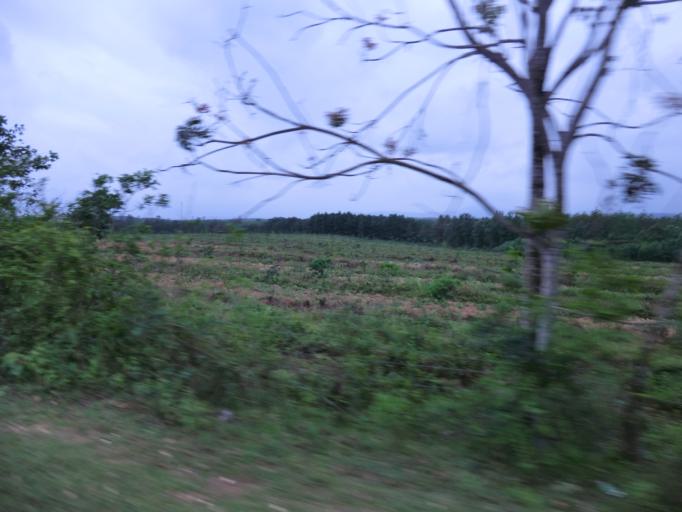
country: VN
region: Quang Tri
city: Cam Lo
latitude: 16.8893
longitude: 106.9924
